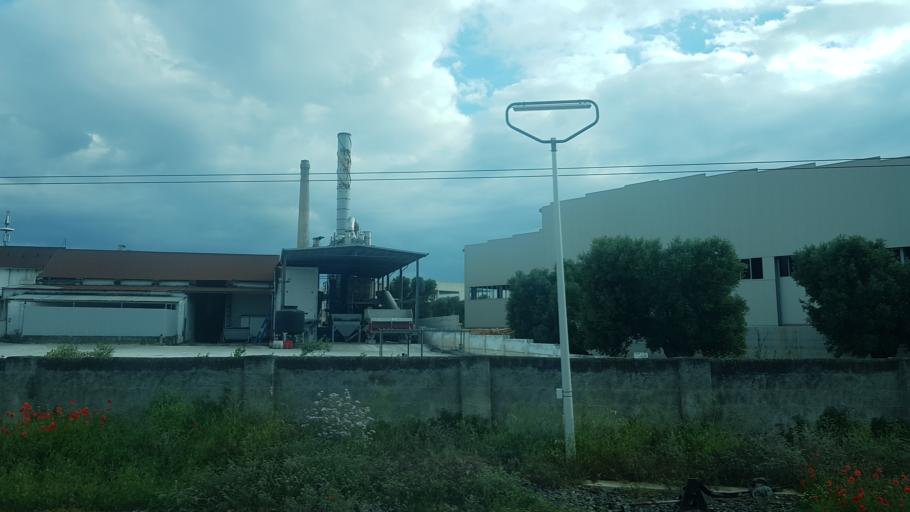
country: IT
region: Apulia
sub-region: Provincia di Brindisi
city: Ostuni
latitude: 40.7532
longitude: 17.5776
